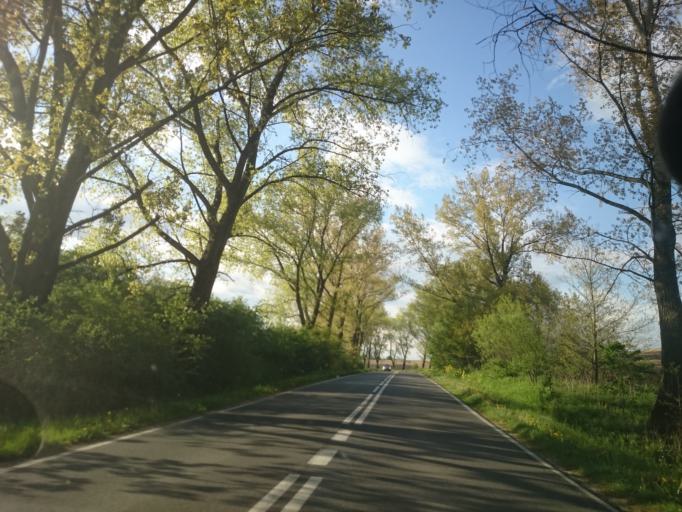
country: PL
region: Lower Silesian Voivodeship
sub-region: Powiat zabkowicki
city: Kamieniec Zabkowicki
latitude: 50.5414
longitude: 16.8642
